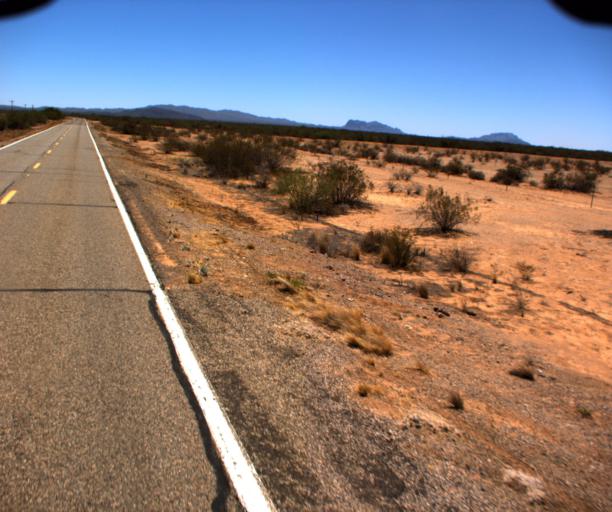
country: US
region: Arizona
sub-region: Pima County
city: Ajo
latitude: 32.1832
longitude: -112.3528
